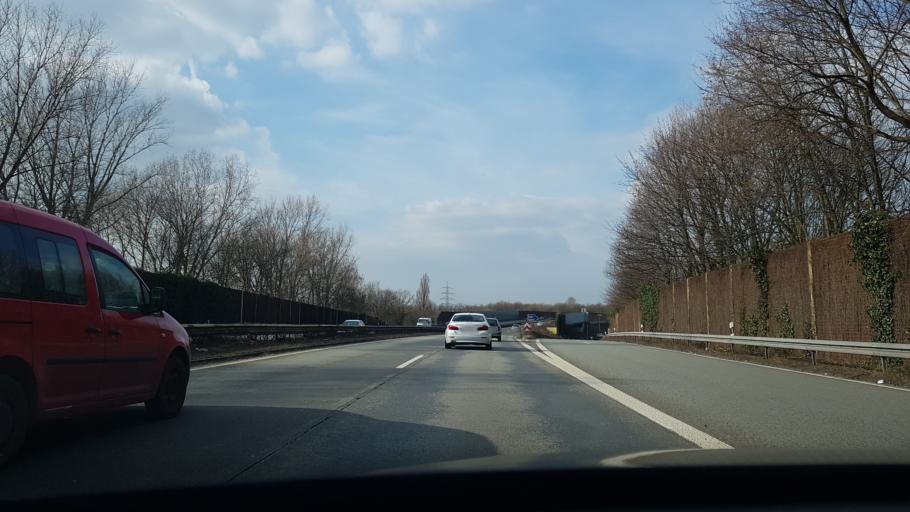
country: DE
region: North Rhine-Westphalia
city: Meiderich
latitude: 51.5078
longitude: 6.7600
